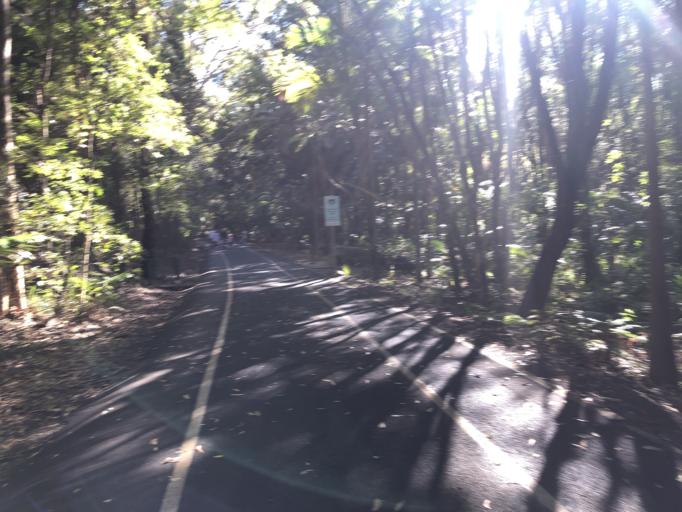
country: AU
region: New South Wales
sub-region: Coffs Harbour
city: Coffs Harbour
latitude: -30.2972
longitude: 153.1250
